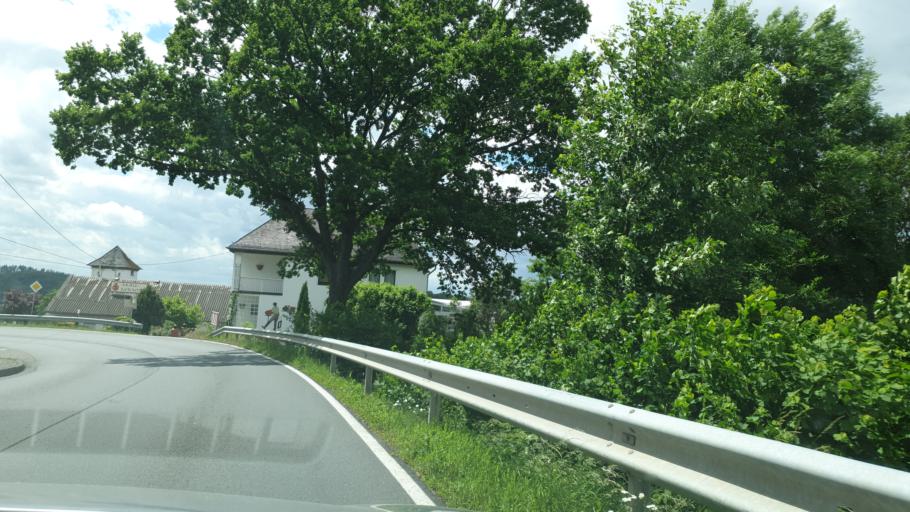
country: DE
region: Rheinland-Pfalz
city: Hillscheid
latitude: 50.4061
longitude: 7.6909
